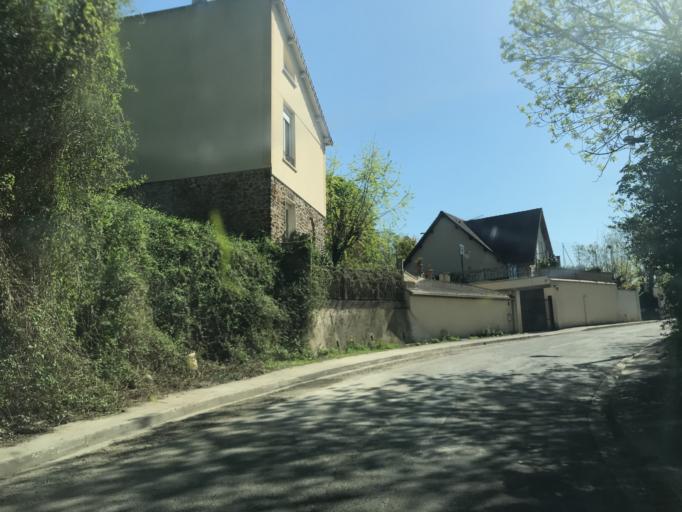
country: FR
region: Ile-de-France
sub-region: Departement du Val-de-Marne
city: Chennevieres-sur-Marne
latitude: 48.7936
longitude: 2.5260
